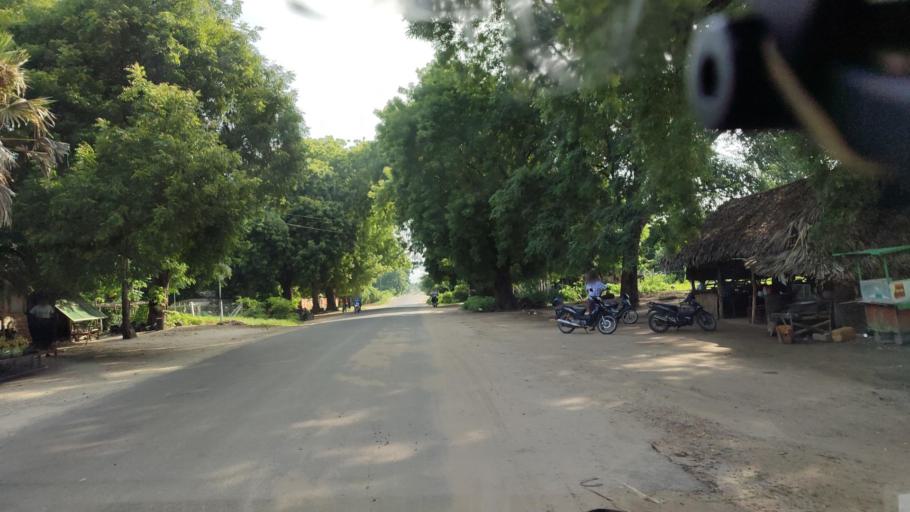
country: MM
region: Magway
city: Pakokku
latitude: 21.2950
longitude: 95.1425
